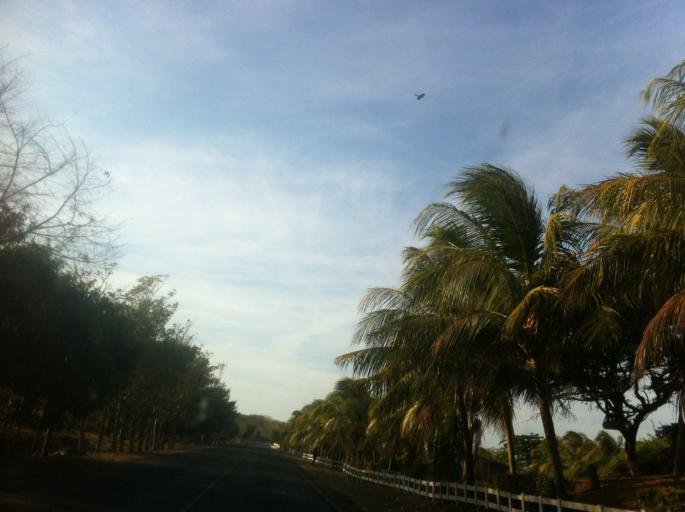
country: NI
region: Rivas
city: San Juan del Sur
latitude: 11.2940
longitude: -85.6843
